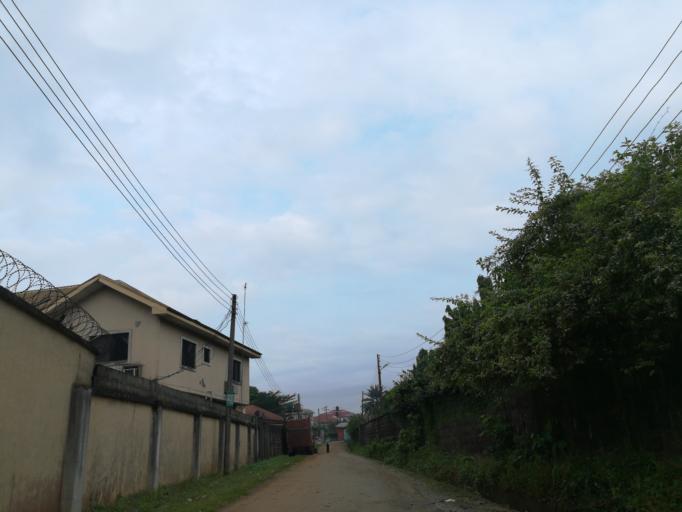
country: NG
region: Rivers
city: Port Harcourt
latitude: 4.8436
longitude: 7.0564
